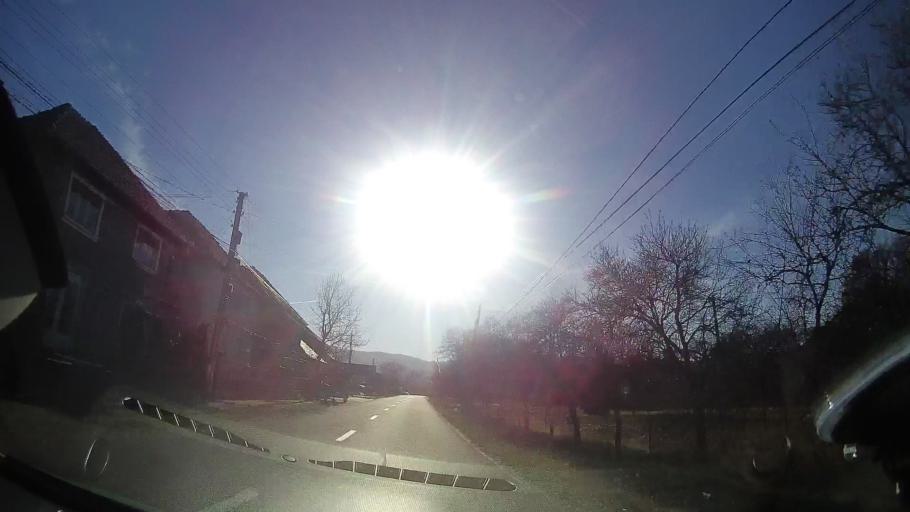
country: RO
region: Bihor
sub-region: Comuna Vadu Crisului
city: Vadu Crisului
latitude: 46.9945
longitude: 22.5220
